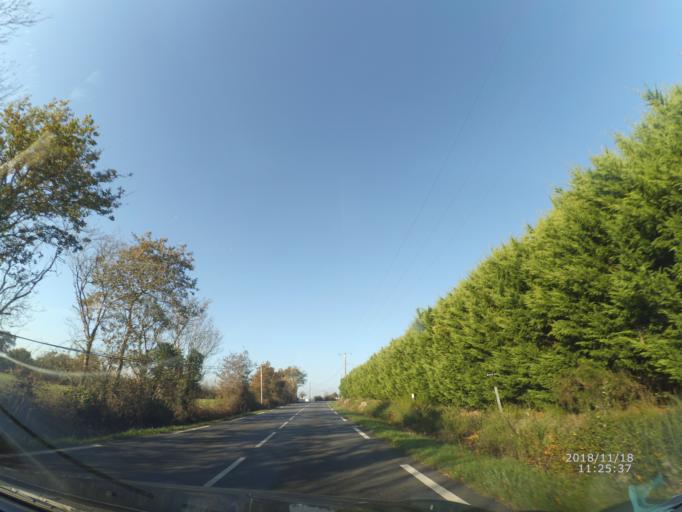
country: FR
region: Pays de la Loire
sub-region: Departement de la Loire-Atlantique
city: Saint-Michel-Chef-Chef
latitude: 47.2215
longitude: -2.1230
